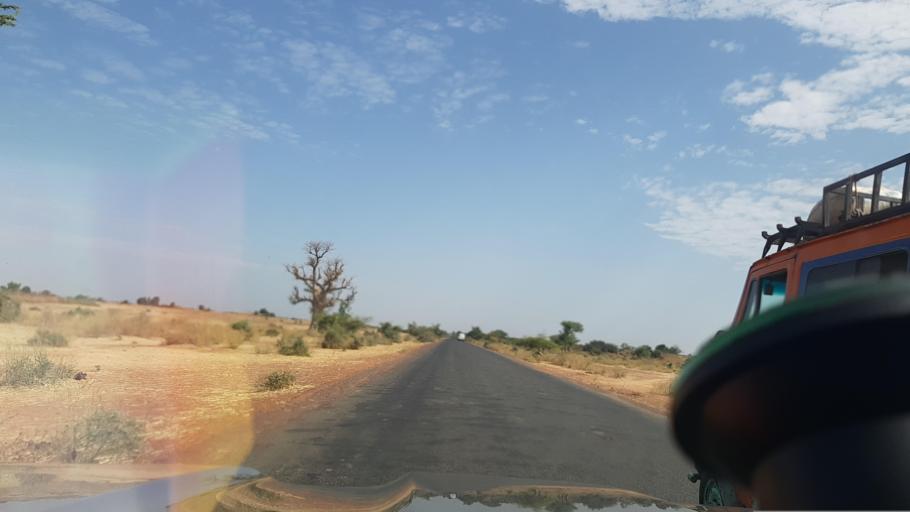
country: ML
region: Segou
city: Markala
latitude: 13.6950
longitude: -6.0983
